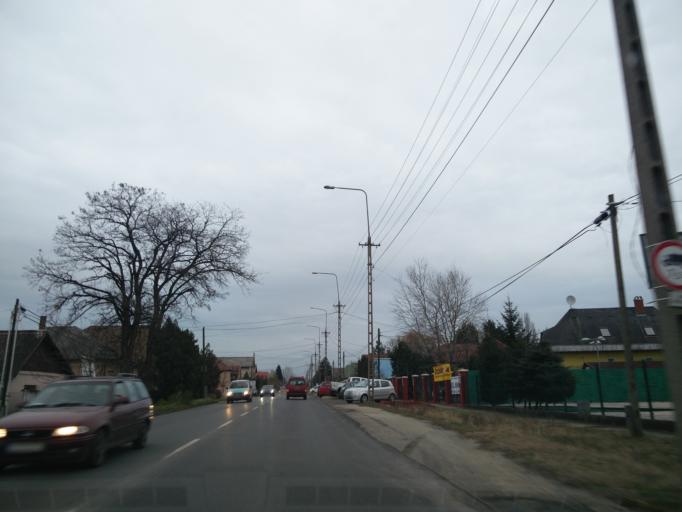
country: HU
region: Pest
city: Ullo
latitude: 47.3901
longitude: 19.3246
